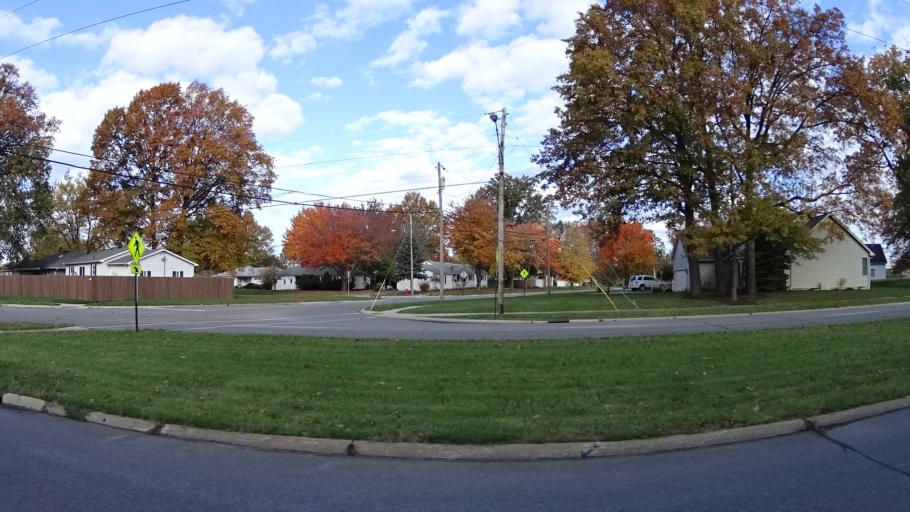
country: US
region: Ohio
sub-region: Lorain County
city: Lorain
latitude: 41.4355
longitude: -82.1791
